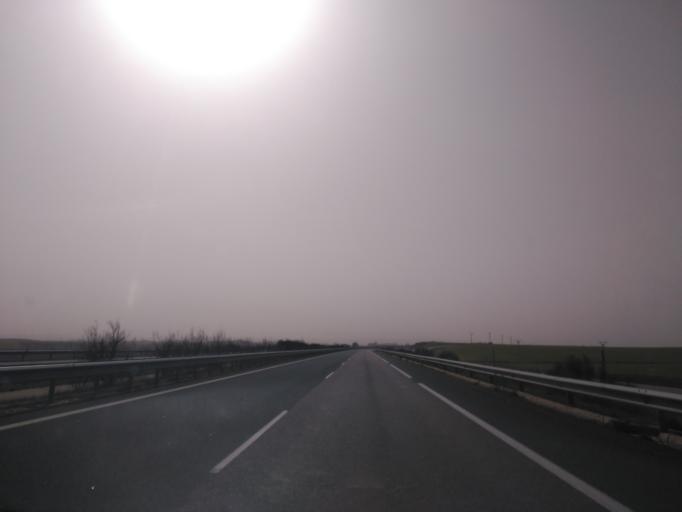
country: ES
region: Castille and Leon
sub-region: Provincia de Palencia
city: Fromista
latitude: 42.2892
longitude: -4.4000
